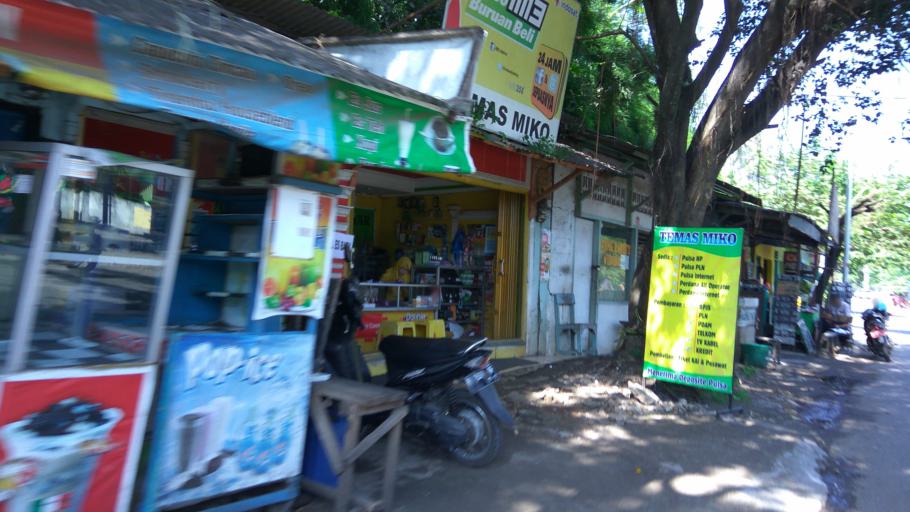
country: ID
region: Central Java
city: Ungaran
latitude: -7.0741
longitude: 110.4138
